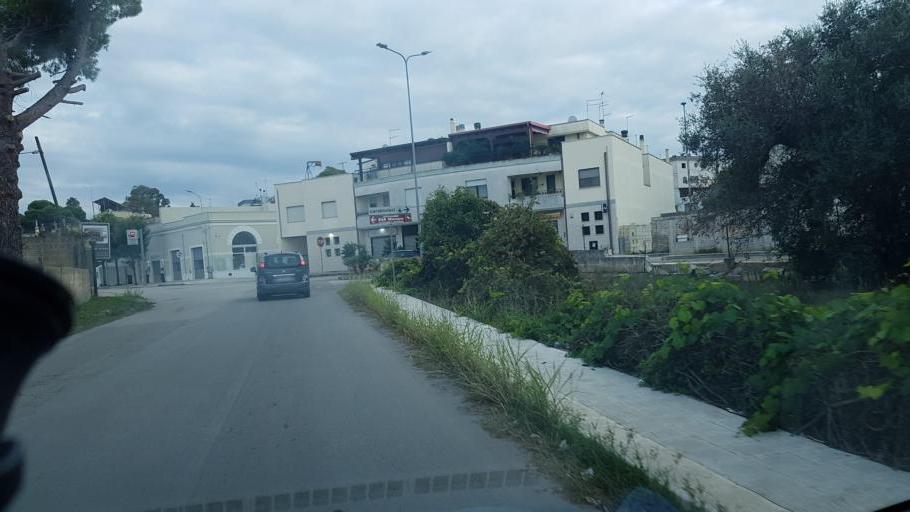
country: IT
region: Apulia
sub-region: Provincia di Brindisi
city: Oria
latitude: 40.5015
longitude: 17.6353
